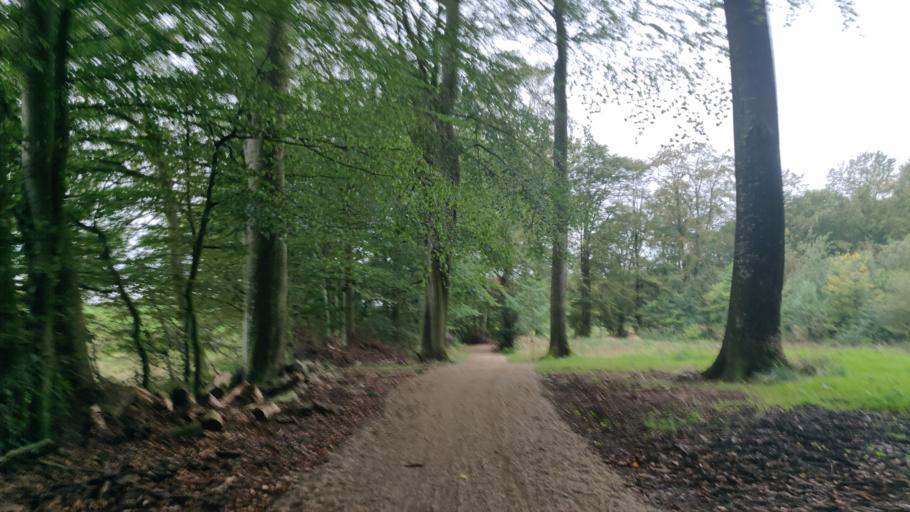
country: DK
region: South Denmark
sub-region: Kolding Kommune
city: Lunderskov
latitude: 55.5390
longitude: 9.3494
